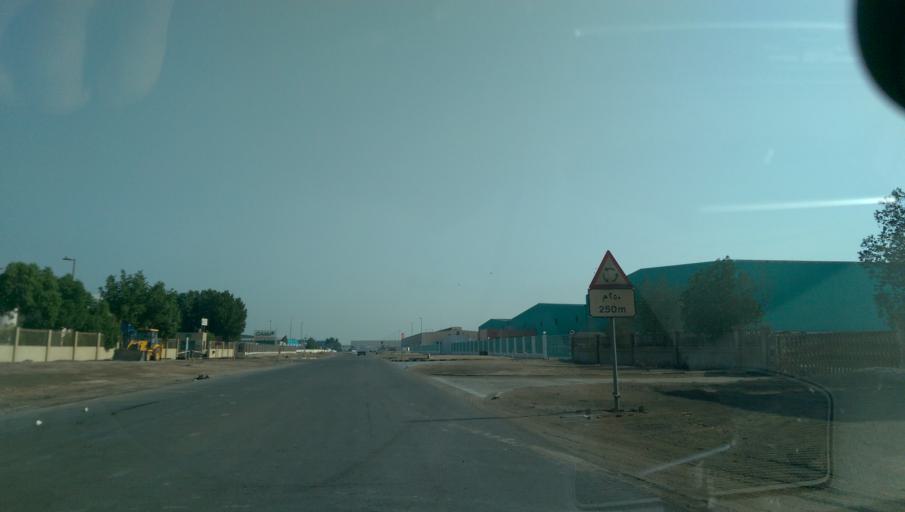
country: AE
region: Abu Dhabi
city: Abu Dhabi
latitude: 24.3257
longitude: 54.4772
